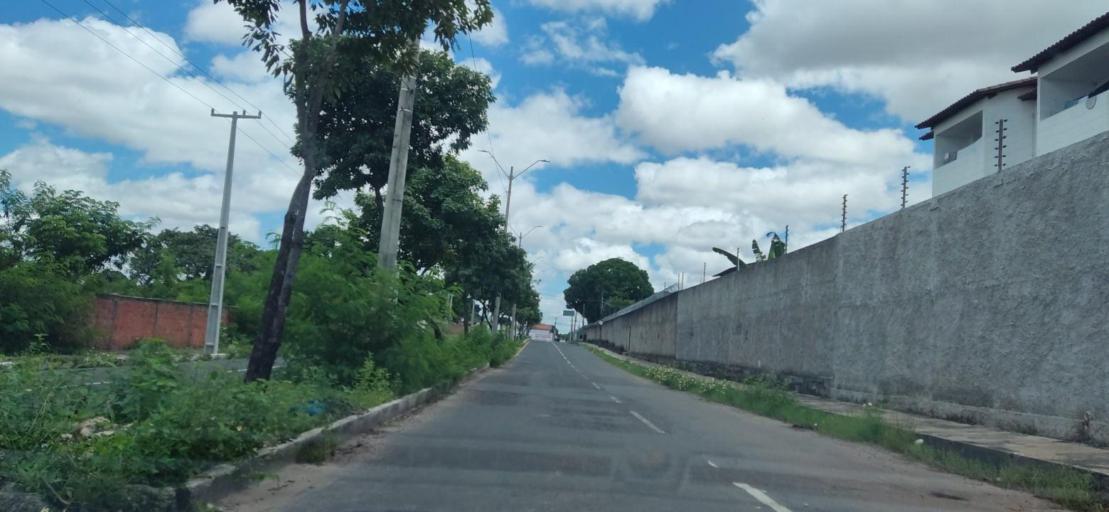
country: BR
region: Piaui
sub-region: Teresina
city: Teresina
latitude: -5.0644
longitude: -42.7574
